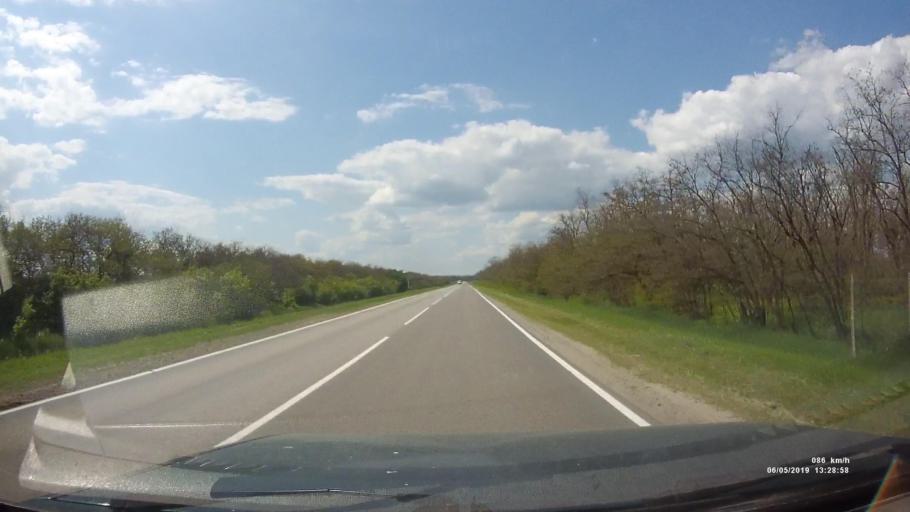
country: RU
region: Rostov
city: Ust'-Donetskiy
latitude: 47.6694
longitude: 40.8529
